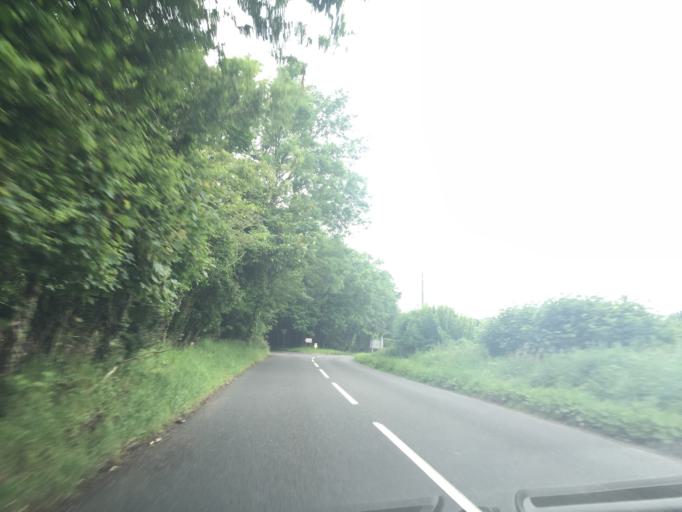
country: GB
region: England
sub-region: Dorset
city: Wool
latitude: 50.6404
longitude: -2.1942
